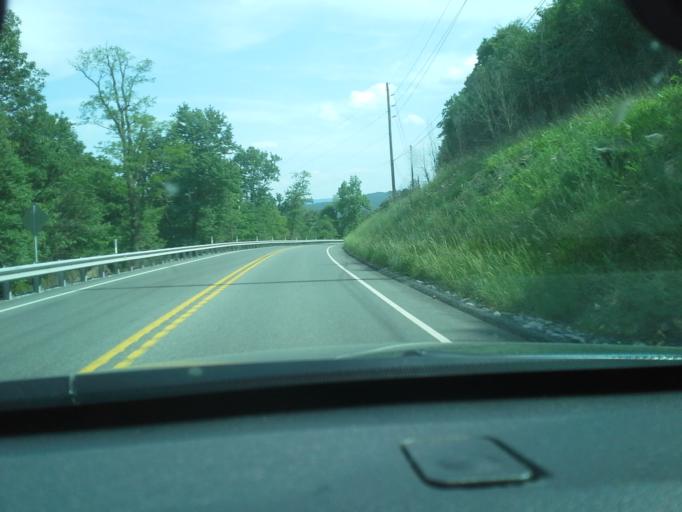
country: US
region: Pennsylvania
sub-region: Fulton County
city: McConnellsburg
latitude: 39.8841
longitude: -77.9659
